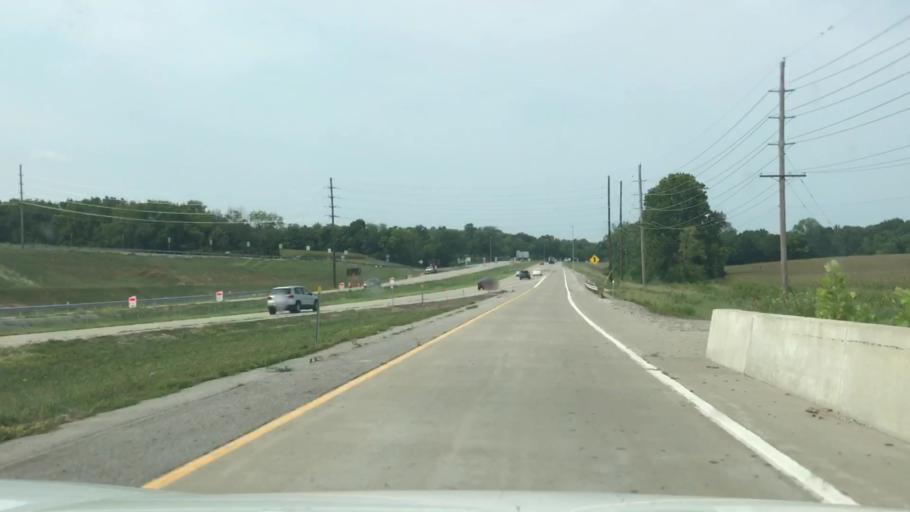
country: US
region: Missouri
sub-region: Saint Charles County
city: Cottleville
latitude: 38.7374
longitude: -90.6371
